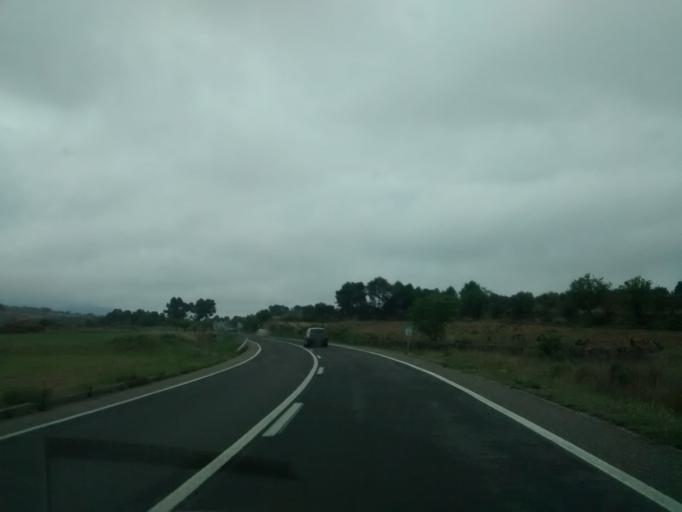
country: ES
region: Catalonia
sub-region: Provincia de Tarragona
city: Bot
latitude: 41.0553
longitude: 0.3607
